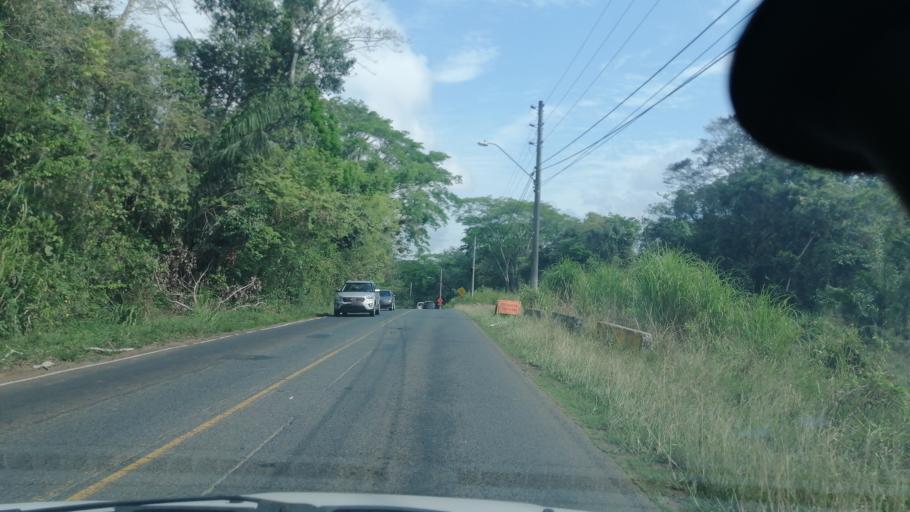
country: PA
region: Panama
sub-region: Distrito de Panama
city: Paraiso
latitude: 9.0430
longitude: -79.6349
